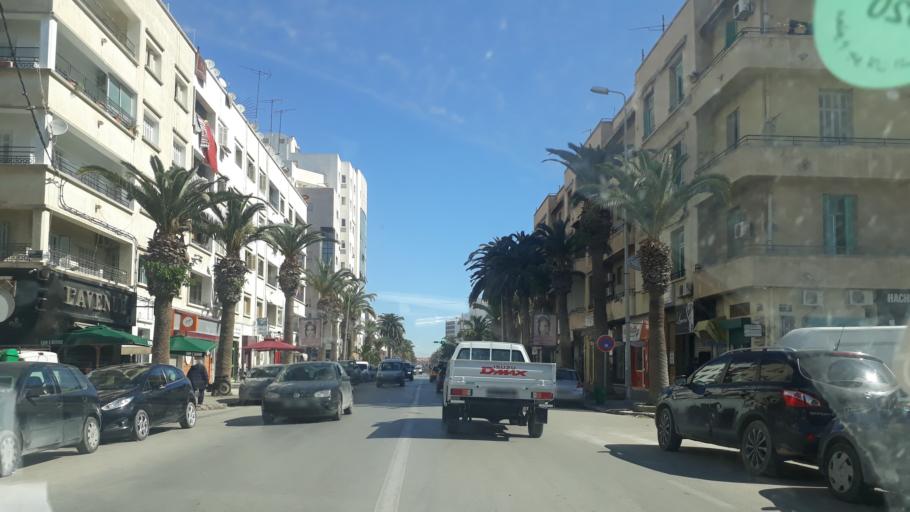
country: TN
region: Safaqis
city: Sfax
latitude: 34.7305
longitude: 10.7610
